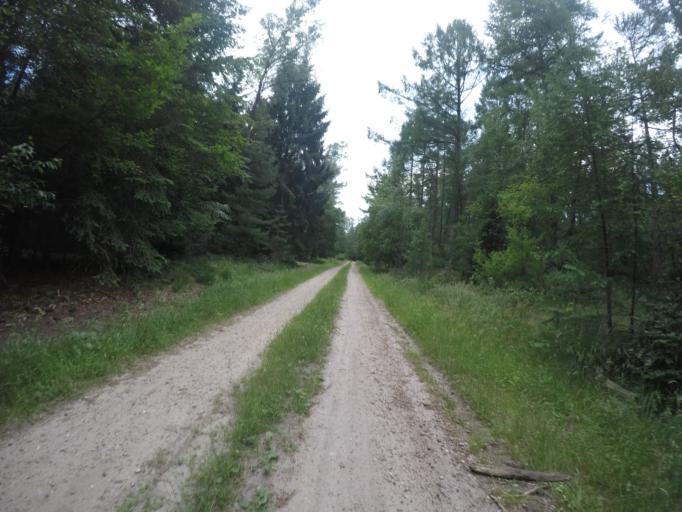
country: DE
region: Lower Saxony
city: Undeloh
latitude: 53.2139
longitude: 9.9766
